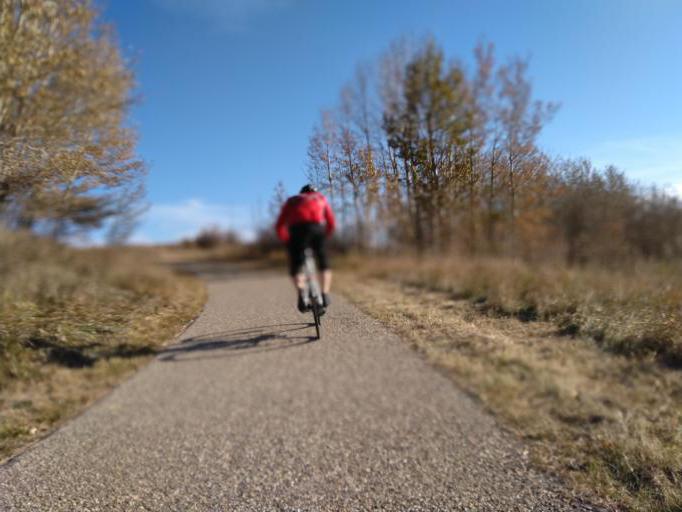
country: CA
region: Alberta
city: Calgary
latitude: 51.1035
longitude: -114.1138
